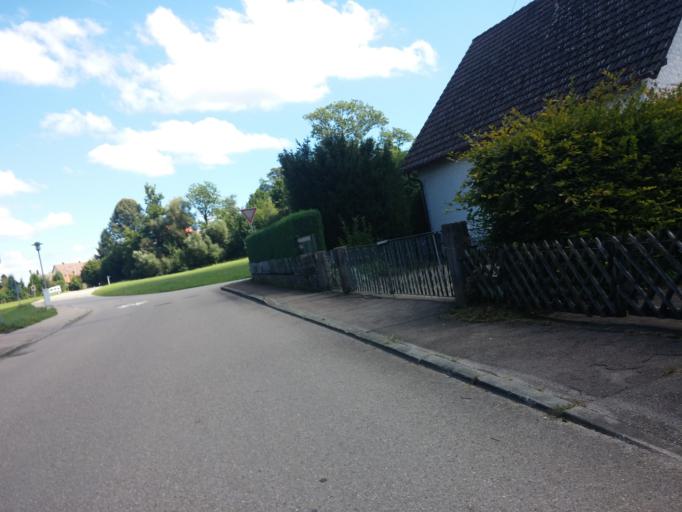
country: DE
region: Bavaria
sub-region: Swabia
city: Woringen
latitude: 47.8782
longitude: 10.2148
